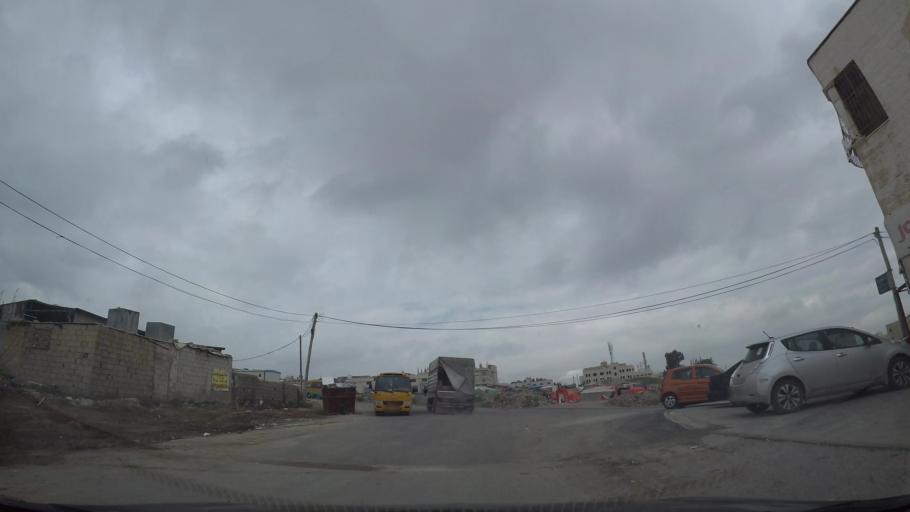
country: JO
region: Amman
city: Wadi as Sir
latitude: 31.9419
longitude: 35.8336
